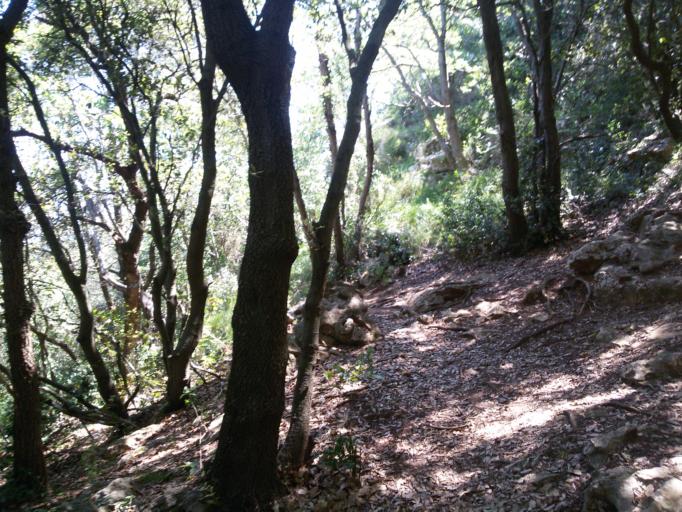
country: IT
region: Liguria
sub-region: Provincia di Savona
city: Borgio
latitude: 44.1727
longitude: 8.3171
